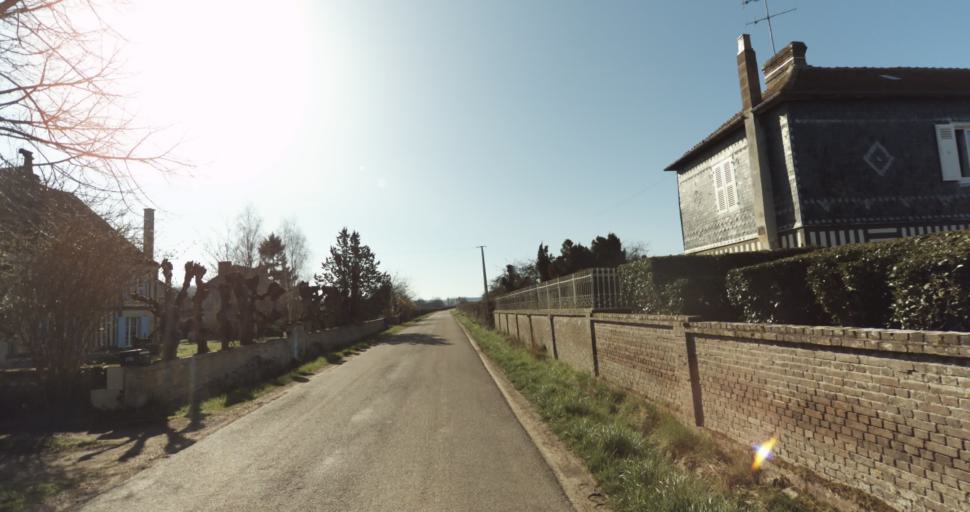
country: FR
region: Lower Normandy
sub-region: Departement du Calvados
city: Saint-Pierre-sur-Dives
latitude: 48.9870
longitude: 0.0298
